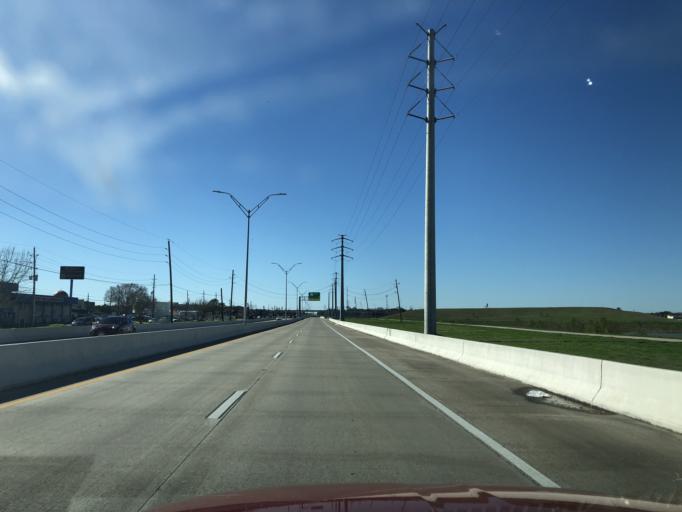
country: US
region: Texas
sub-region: Fort Bend County
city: Mission Bend
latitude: 29.7114
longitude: -95.6344
